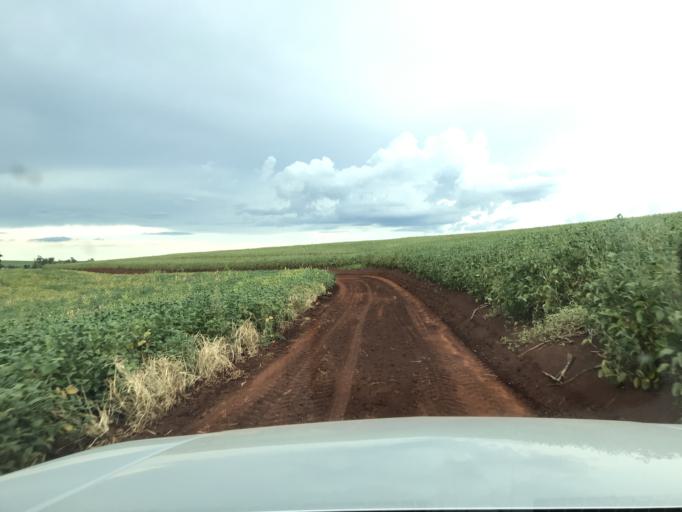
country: BR
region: Parana
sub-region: Palotina
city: Palotina
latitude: -24.2704
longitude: -53.7716
